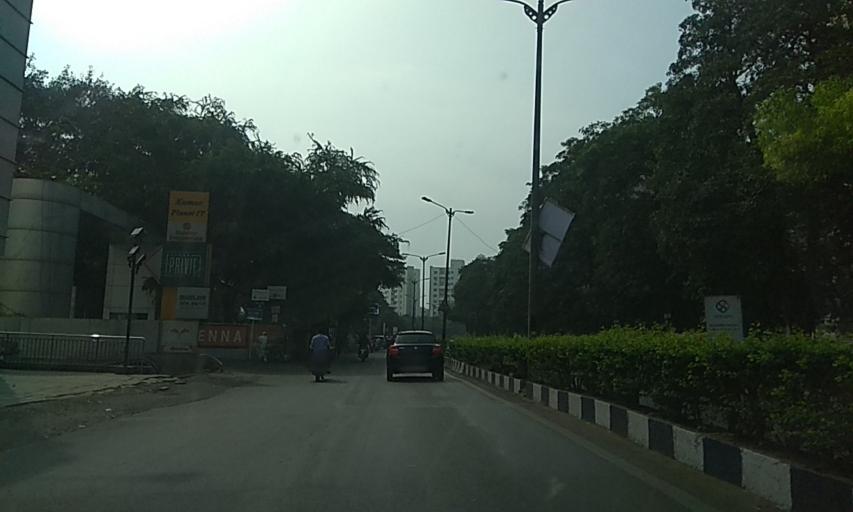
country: IN
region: Maharashtra
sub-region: Pune Division
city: Pune
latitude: 18.5125
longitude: 73.9325
